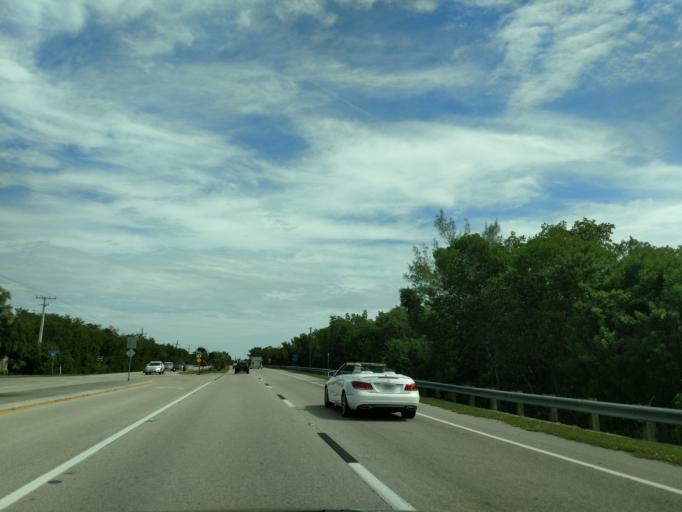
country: US
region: Florida
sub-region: Lee County
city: Punta Rassa
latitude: 26.4888
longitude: -81.9888
